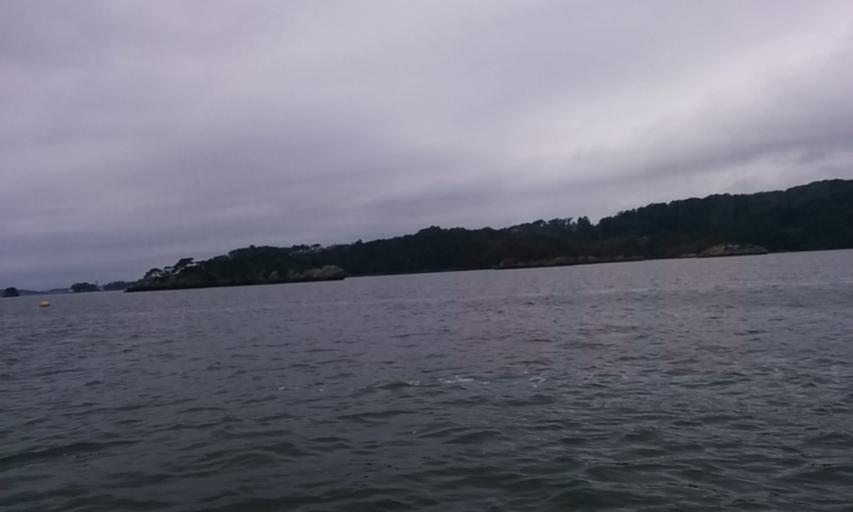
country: JP
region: Miyagi
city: Matsushima
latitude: 38.3580
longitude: 141.0721
